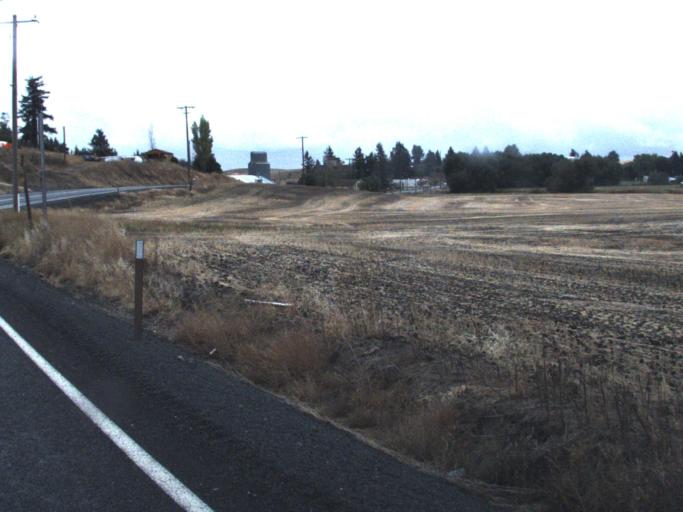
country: US
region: Washington
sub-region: Whitman County
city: Colfax
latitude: 47.1355
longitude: -117.2434
